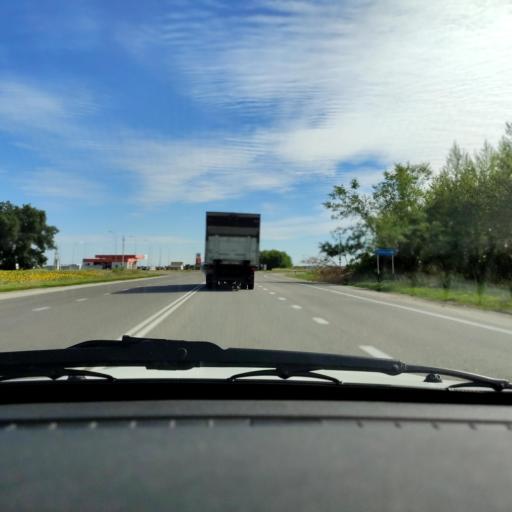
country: RU
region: Voronezj
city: Orlovo
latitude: 51.7342
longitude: 39.5630
